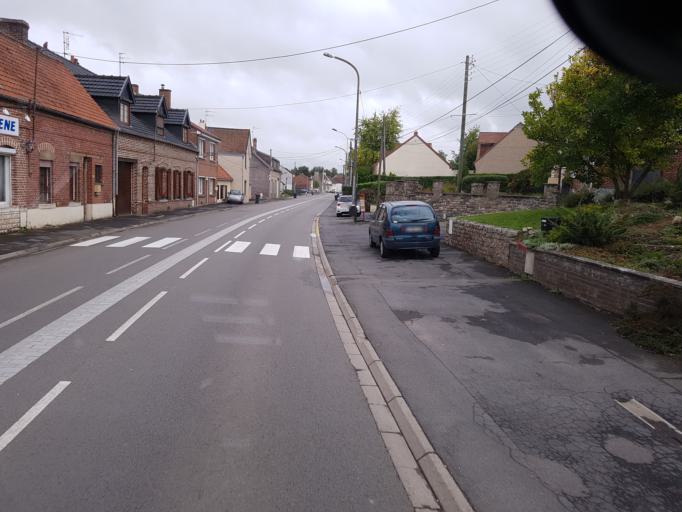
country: FR
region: Nord-Pas-de-Calais
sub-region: Departement du Pas-de-Calais
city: Souchez
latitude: 50.3960
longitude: 2.7482
